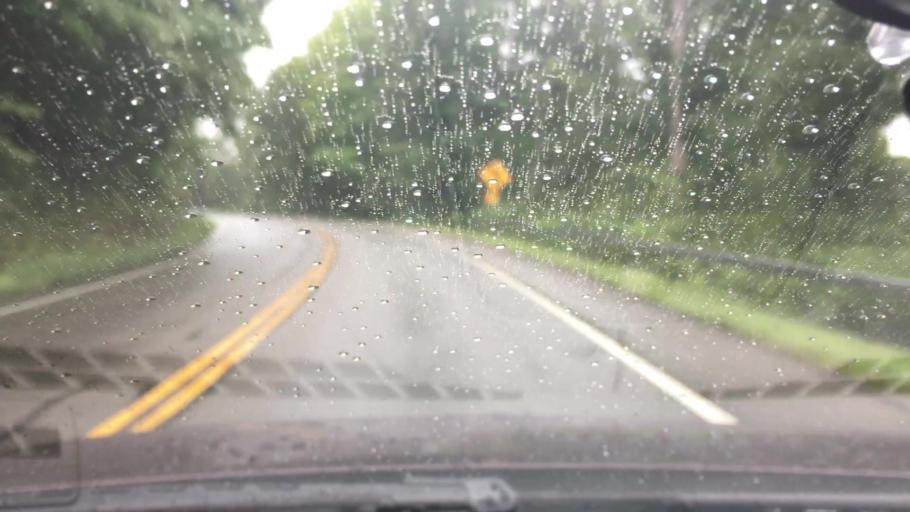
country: US
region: New York
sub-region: Dutchess County
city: Brinckerhoff
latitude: 41.5665
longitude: -73.8226
